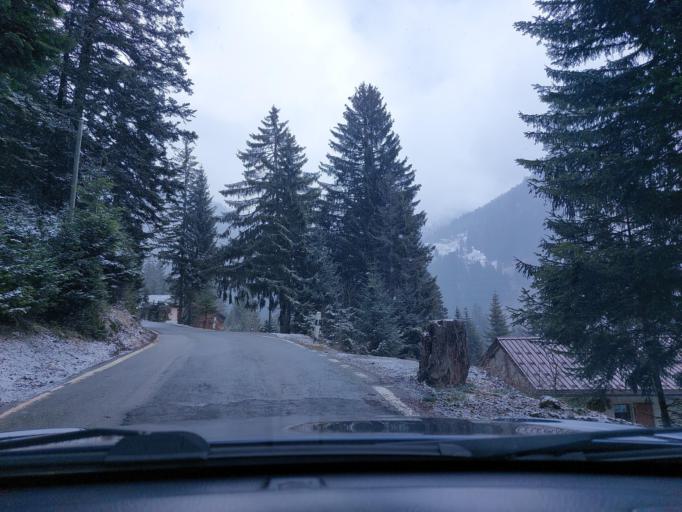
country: CH
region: Valais
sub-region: Sion District
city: Saviese
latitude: 46.2959
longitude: 7.3256
